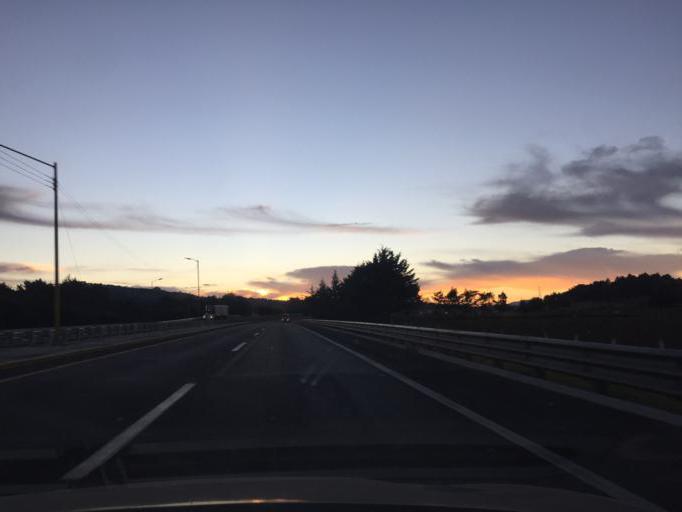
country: MX
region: Puebla
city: San Jose Esperanza
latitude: 18.8602
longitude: -97.3633
